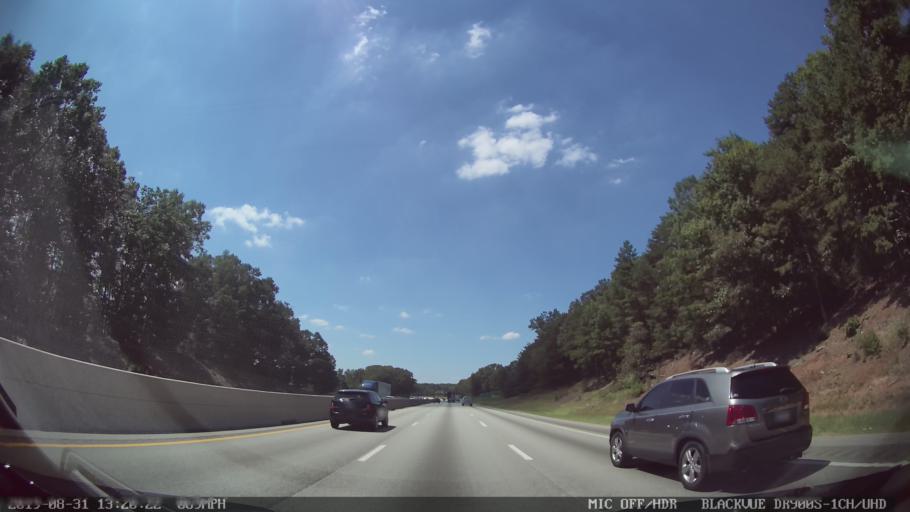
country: US
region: South Carolina
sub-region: Spartanburg County
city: Duncan
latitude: 34.9003
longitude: -82.1430
